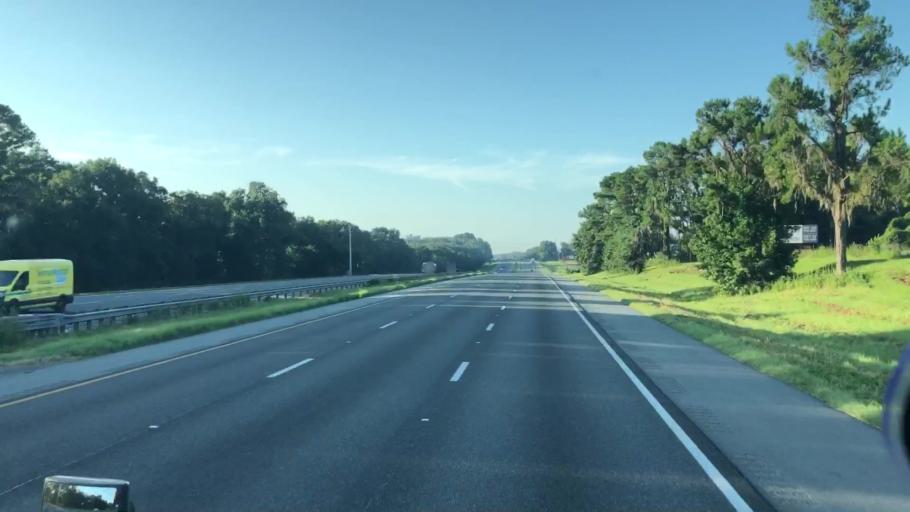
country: US
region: Florida
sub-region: Marion County
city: Citra
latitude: 29.3112
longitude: -82.2088
